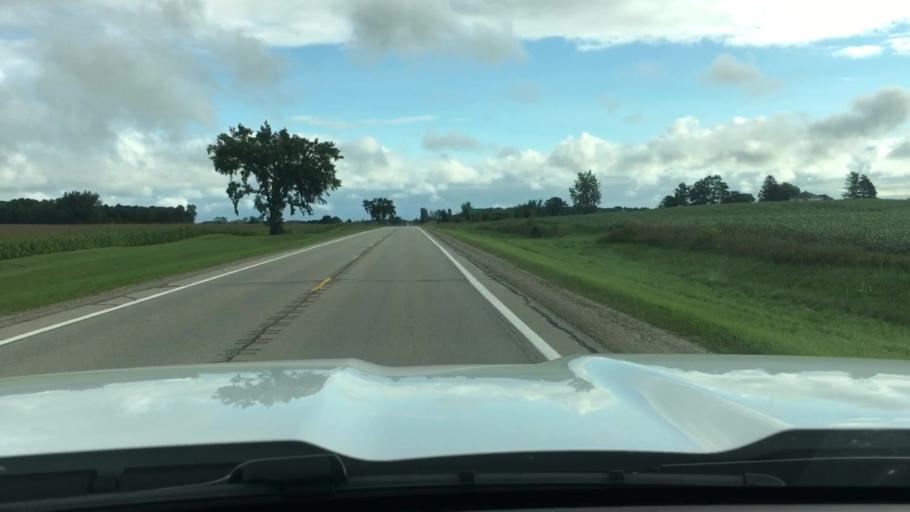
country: US
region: Michigan
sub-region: Tuscola County
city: Caro
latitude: 43.5668
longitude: -83.3053
